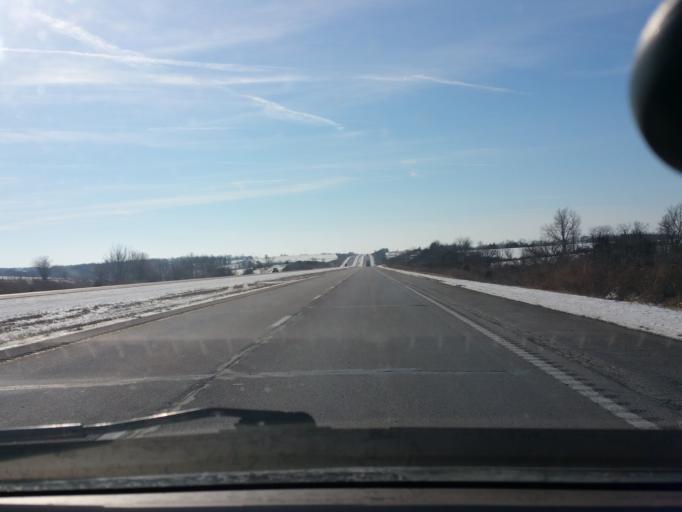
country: US
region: Iowa
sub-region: Decatur County
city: Lamoni
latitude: 40.5128
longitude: -93.9641
